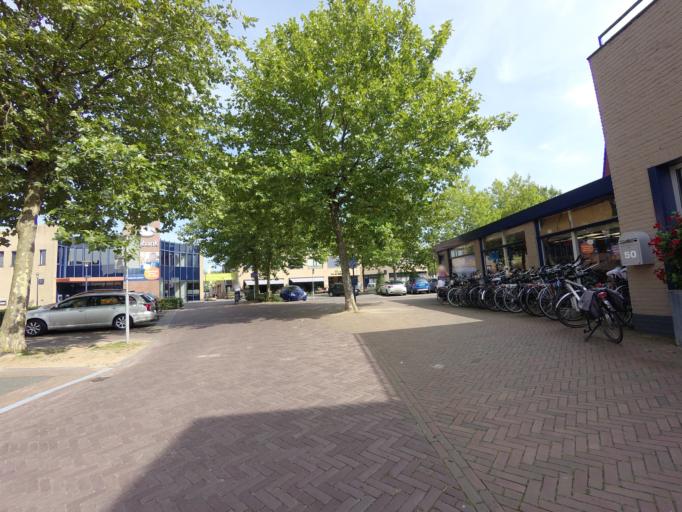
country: NL
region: Overijssel
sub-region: Gemeente Tubbergen
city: Tubbergen
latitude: 52.4071
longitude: 6.7821
